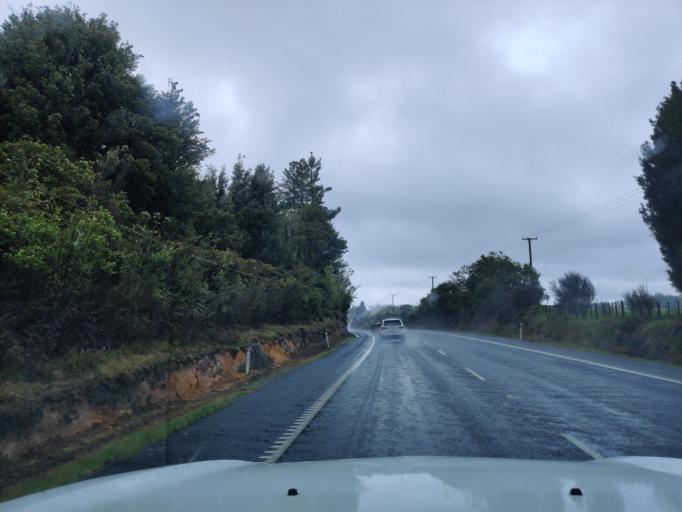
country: NZ
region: Bay of Plenty
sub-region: Rotorua District
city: Rotorua
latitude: -38.0595
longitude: 176.0928
